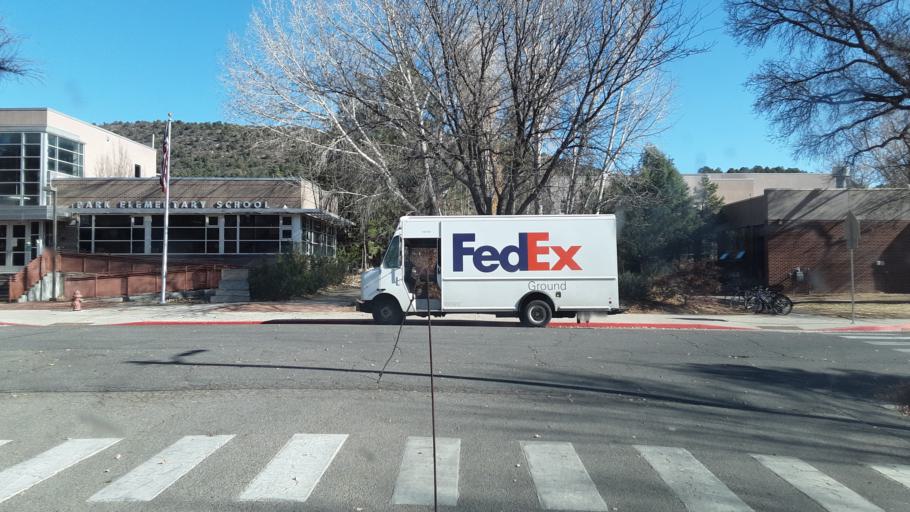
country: US
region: Colorado
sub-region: La Plata County
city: Durango
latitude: 37.2677
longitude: -107.8756
